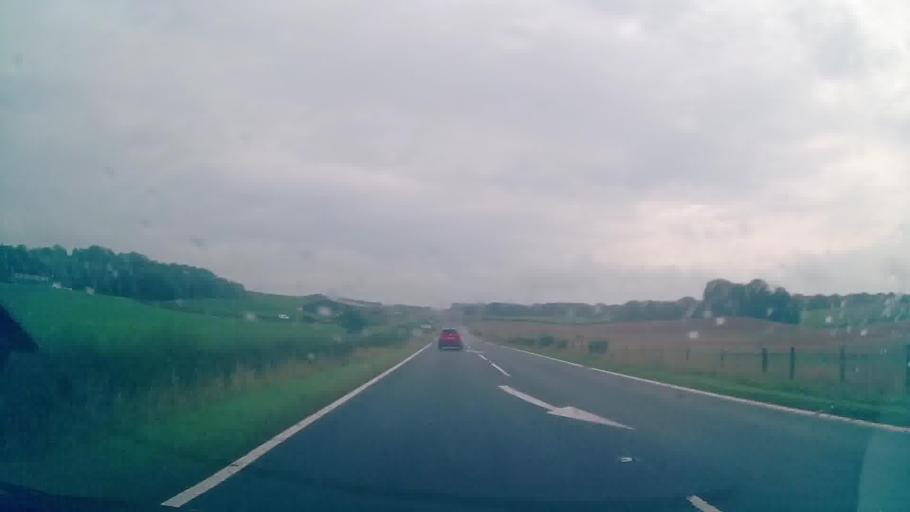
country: GB
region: Scotland
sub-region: Dumfries and Galloway
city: Lochmaben
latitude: 55.0448
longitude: -3.4503
